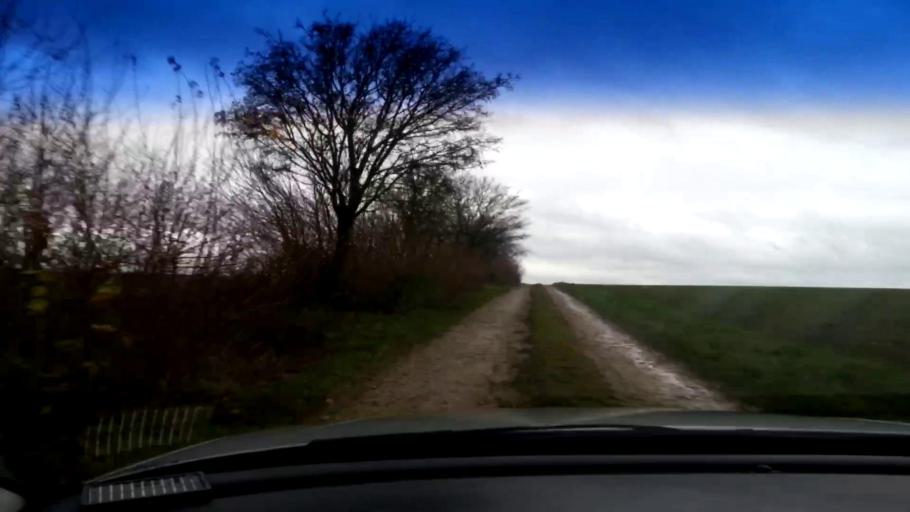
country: DE
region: Bavaria
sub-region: Upper Franconia
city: Ebensfeld
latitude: 50.0327
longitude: 10.9909
